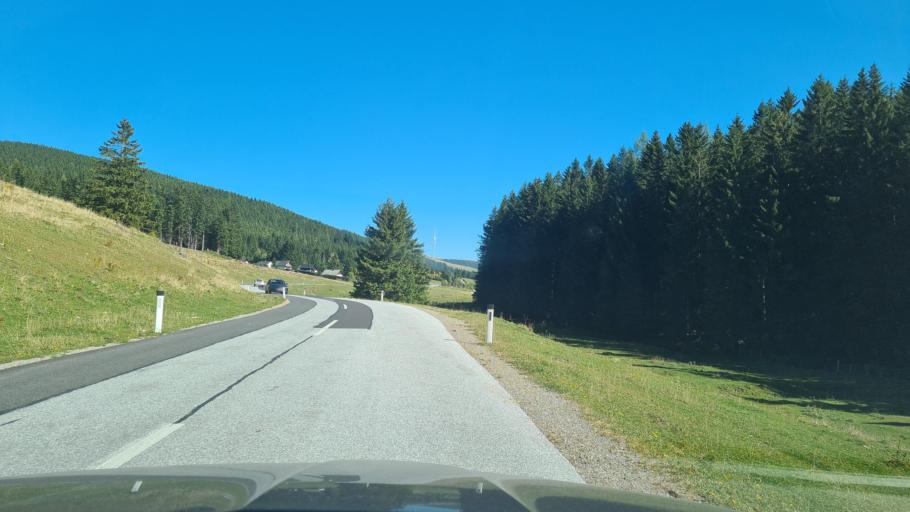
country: AT
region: Styria
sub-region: Politischer Bezirk Weiz
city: Passail
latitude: 47.3528
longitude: 15.5004
